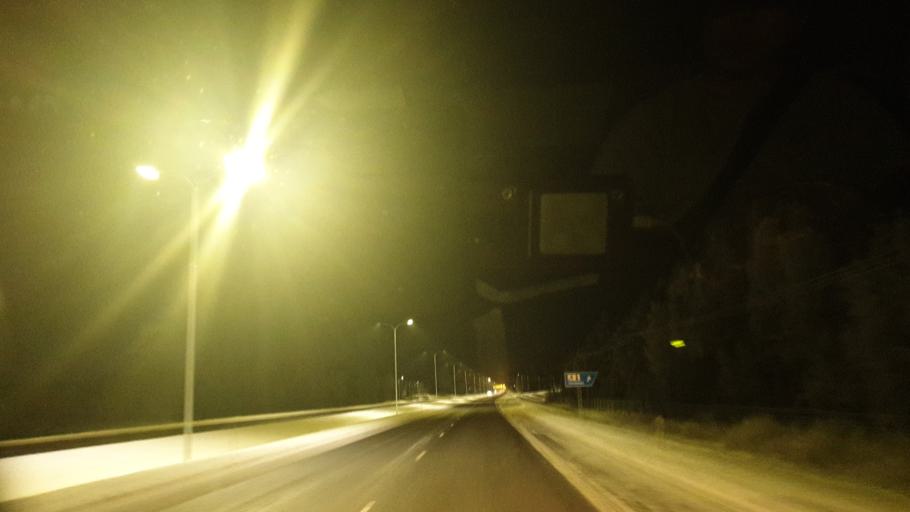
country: FI
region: Northern Ostrobothnia
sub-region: Oulu
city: Haukipudas
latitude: 65.1357
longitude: 25.4329
